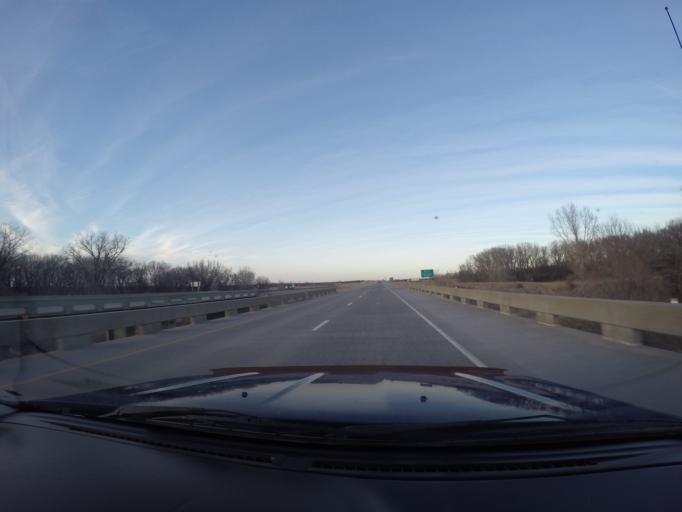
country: US
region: Kansas
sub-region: McPherson County
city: Lindsborg
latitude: 38.6124
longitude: -97.6212
